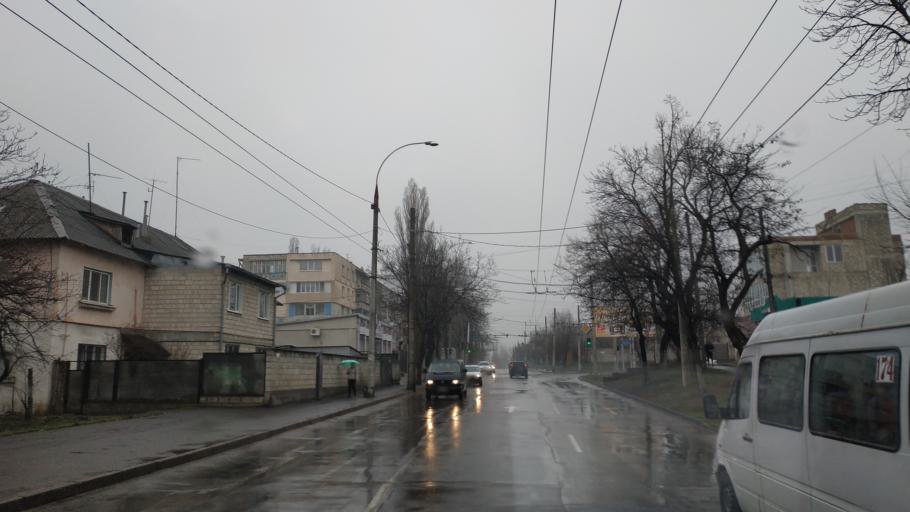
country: MD
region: Chisinau
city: Chisinau
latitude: 47.0232
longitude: 28.7933
